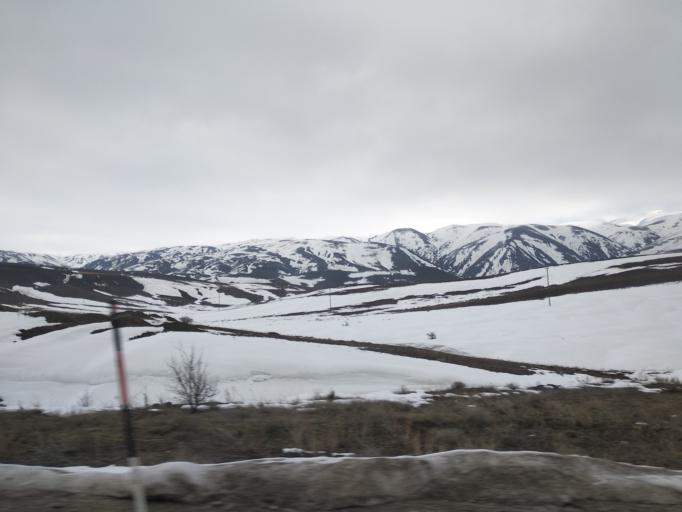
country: TR
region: Erzincan
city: Catalarmut
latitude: 39.8282
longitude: 39.3875
